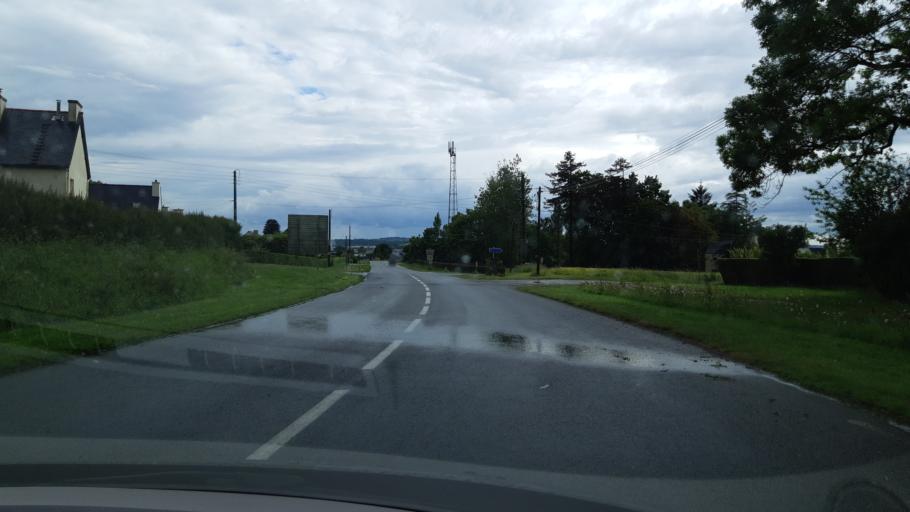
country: FR
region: Brittany
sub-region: Departement du Finistere
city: Landivisiau
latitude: 48.5261
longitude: -4.0682
